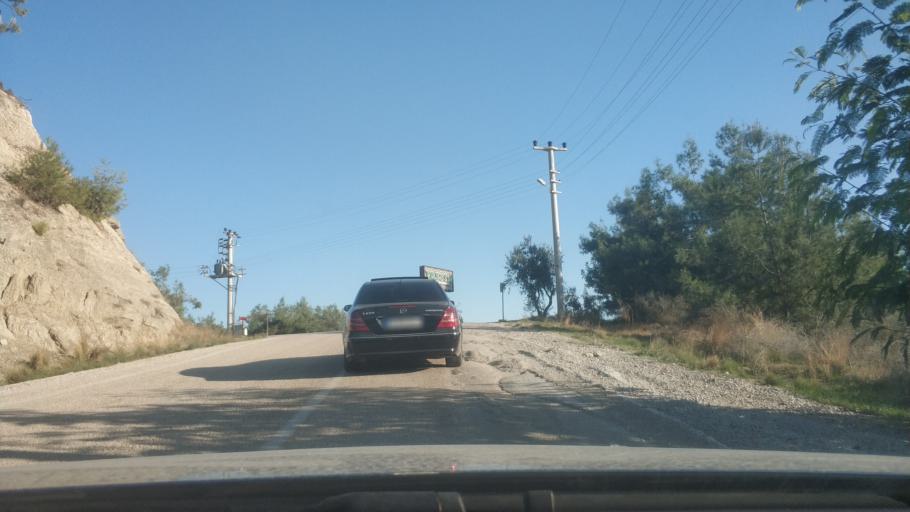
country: TR
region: Adana
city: Adana
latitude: 37.0996
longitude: 35.2896
